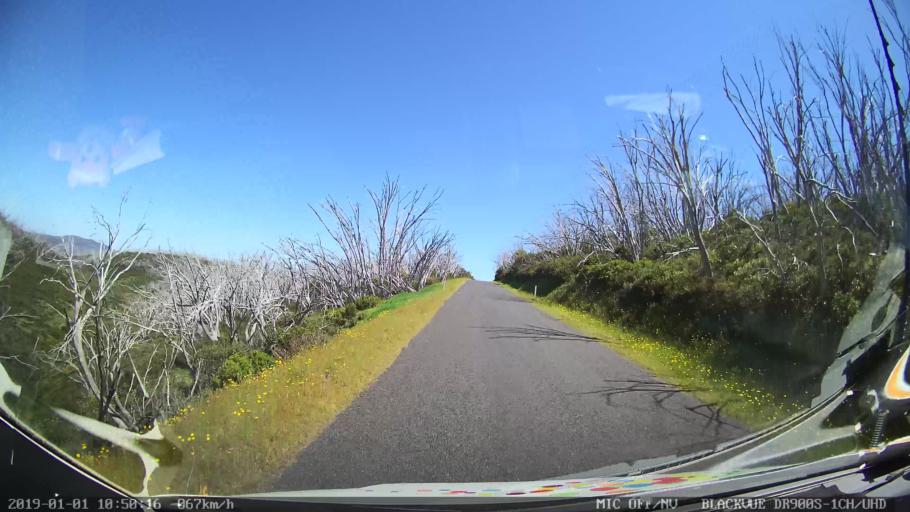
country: AU
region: New South Wales
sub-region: Snowy River
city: Jindabyne
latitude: -36.0298
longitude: 148.3720
